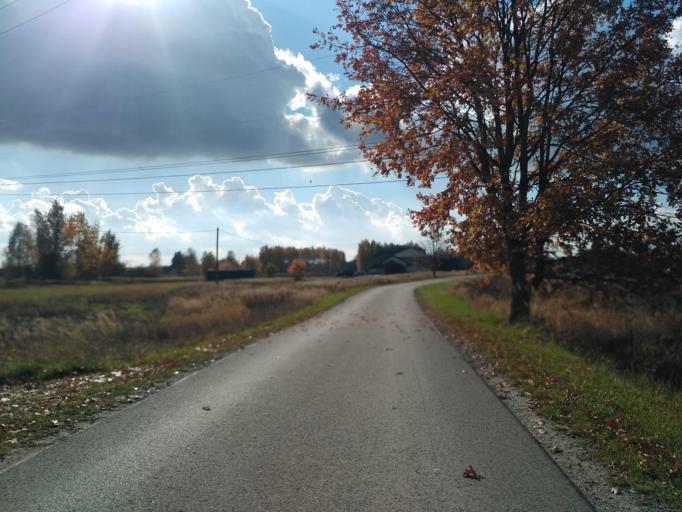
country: PL
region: Subcarpathian Voivodeship
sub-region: Powiat rzeszowski
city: Swilcza
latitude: 50.1235
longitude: 21.9065
